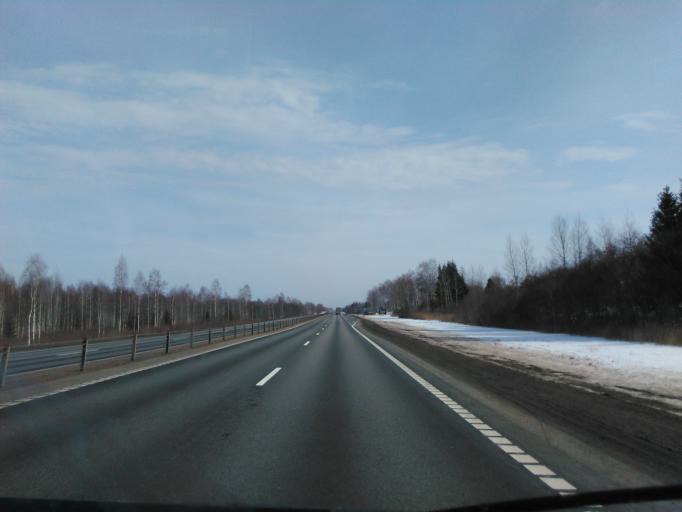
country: BY
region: Vitebsk
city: Dubrowna
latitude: 54.6894
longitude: 30.8996
